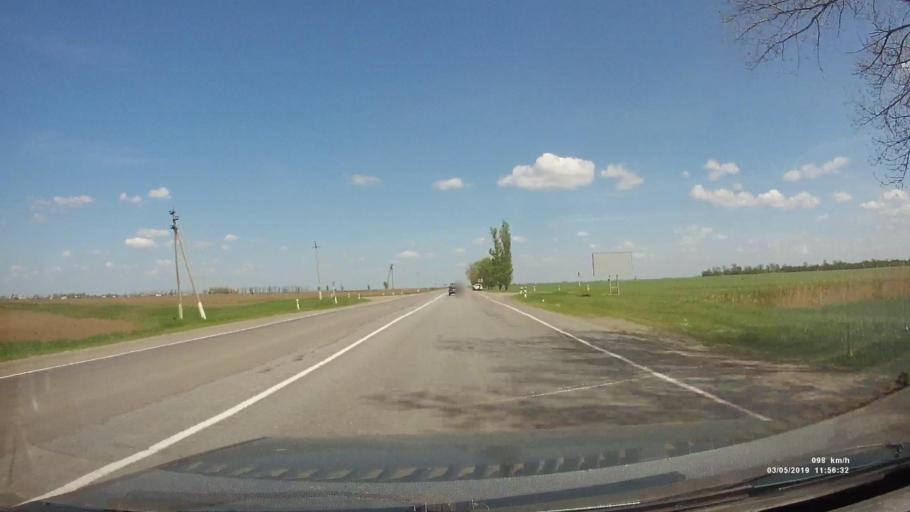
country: RU
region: Rostov
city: Bagayevskaya
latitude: 47.1958
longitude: 40.3019
